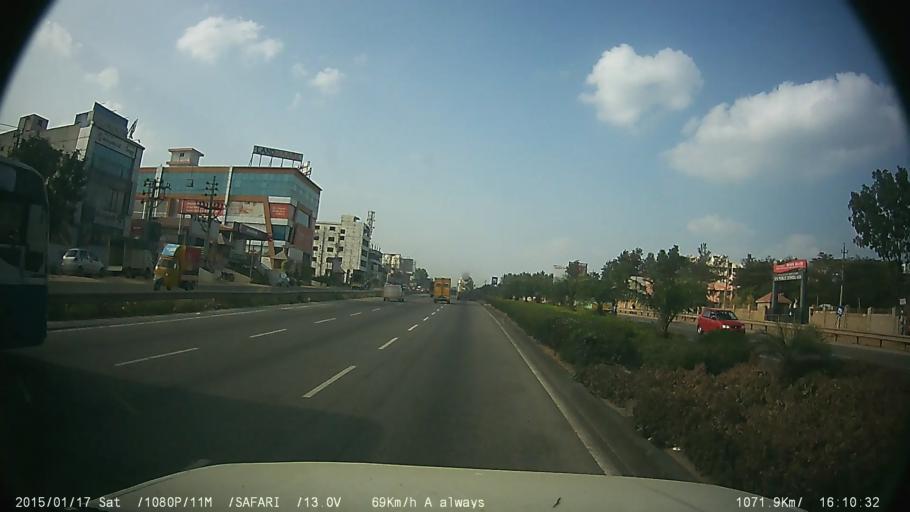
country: IN
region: Karnataka
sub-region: Bangalore Urban
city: Anekal
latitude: 12.8330
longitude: 77.6803
